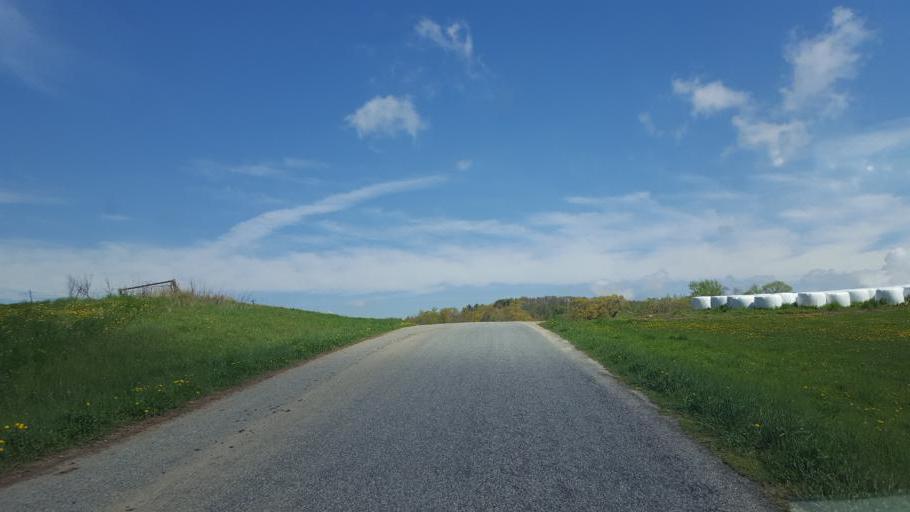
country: US
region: Wisconsin
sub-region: Vernon County
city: Hillsboro
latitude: 43.6864
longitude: -90.3176
